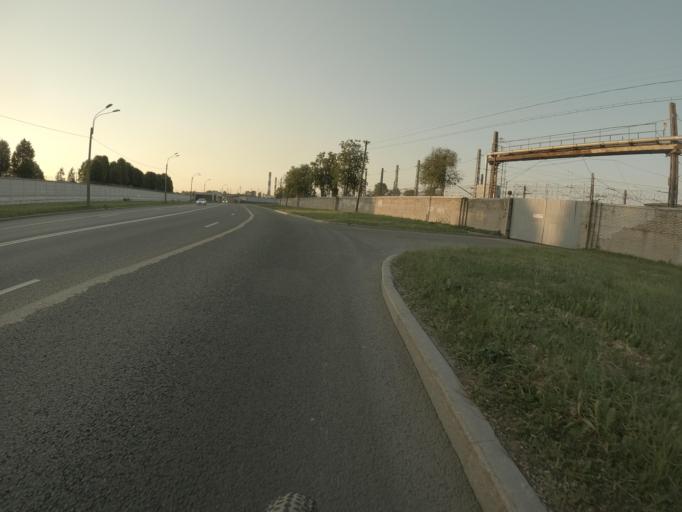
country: RU
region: St.-Petersburg
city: Avtovo
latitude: 59.8576
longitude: 30.2833
